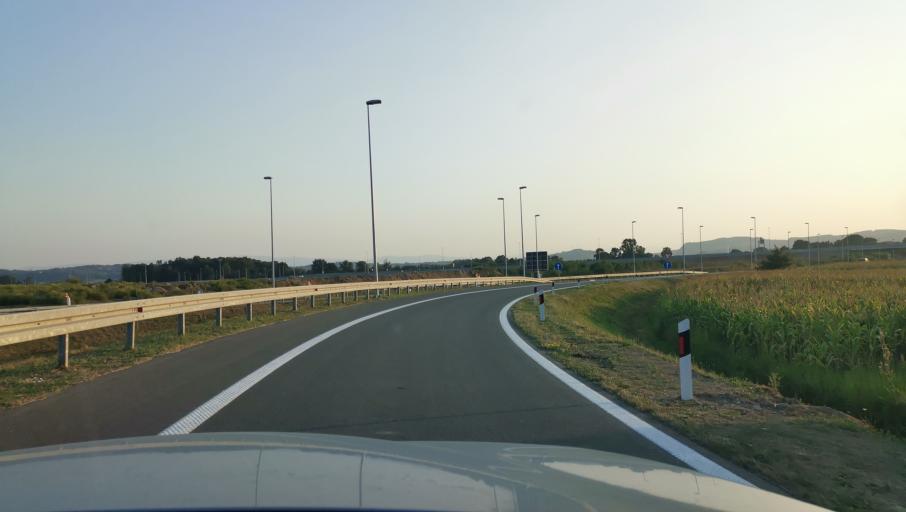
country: RS
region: Central Serbia
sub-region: Kolubarski Okrug
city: Lajkovac
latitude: 44.3625
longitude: 20.1286
